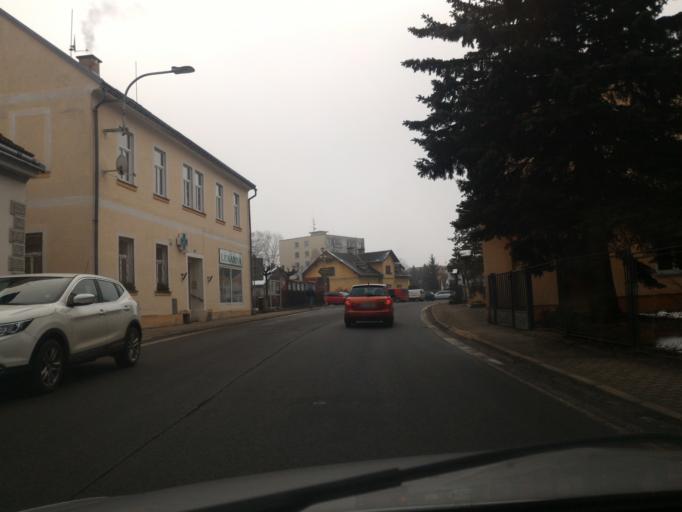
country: CZ
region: Liberecky
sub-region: Okres Liberec
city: Hejnice
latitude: 50.8788
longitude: 15.1818
